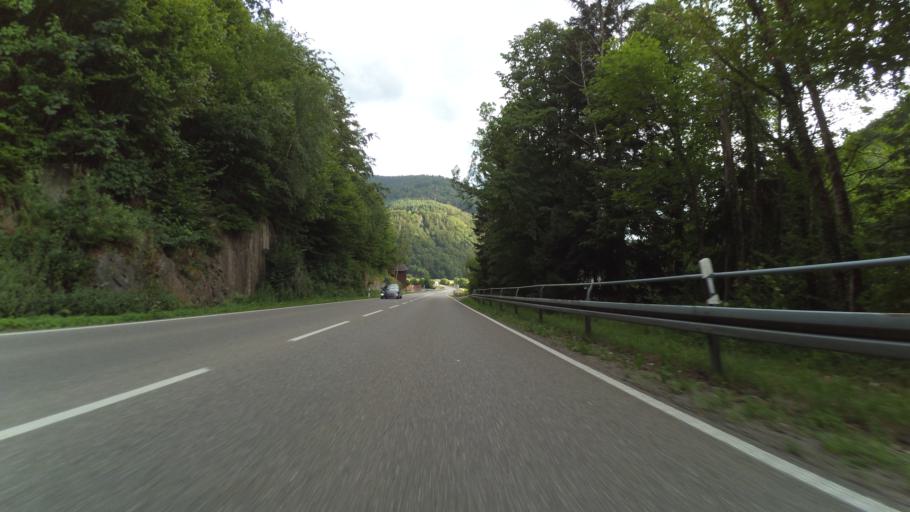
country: DE
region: Baden-Wuerttemberg
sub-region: Freiburg Region
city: Utzenfeld
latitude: 47.8091
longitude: 7.9360
